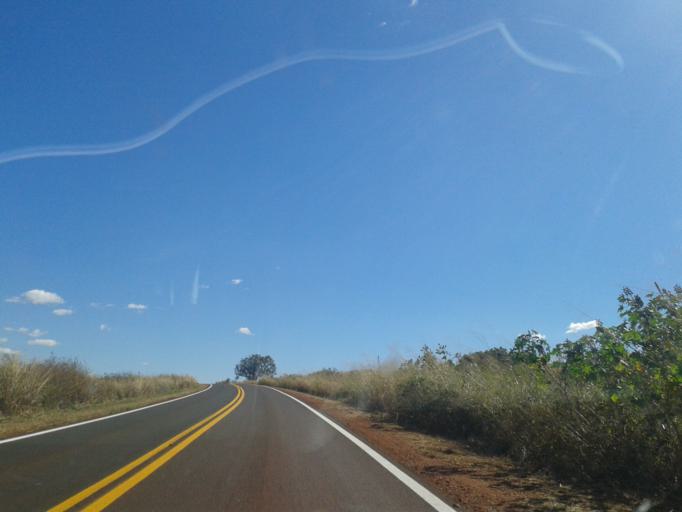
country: BR
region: Minas Gerais
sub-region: Capinopolis
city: Capinopolis
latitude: -18.6913
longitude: -49.4644
